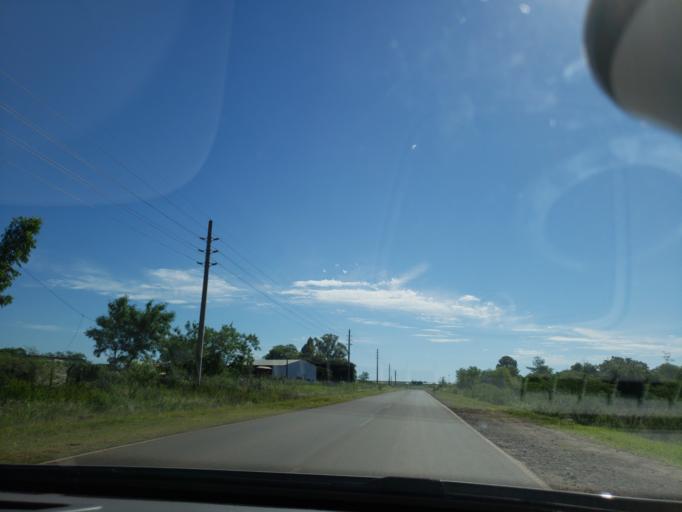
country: AR
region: Misiones
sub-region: Departamento de Capital
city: Posadas
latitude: -27.3870
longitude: -55.9755
